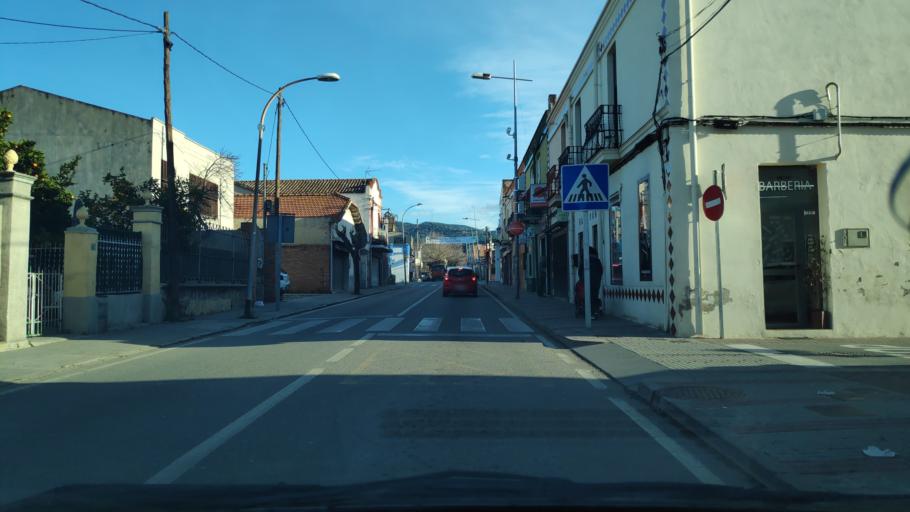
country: ES
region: Catalonia
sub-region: Provincia de Barcelona
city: Mollet del Valles
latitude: 41.5276
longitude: 2.2259
